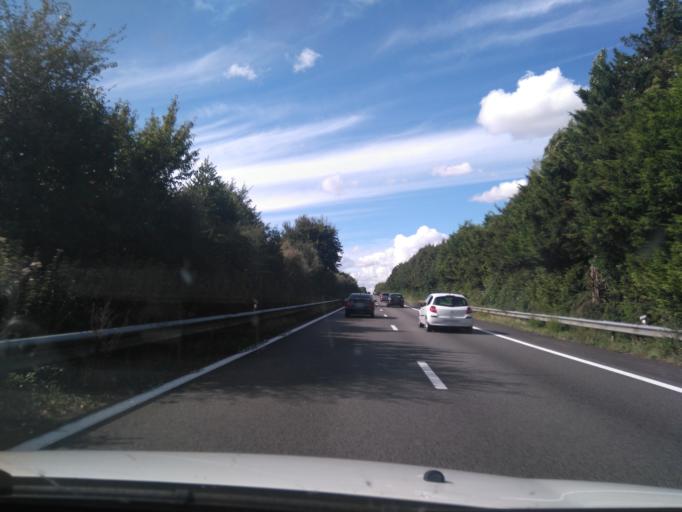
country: FR
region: Pays de la Loire
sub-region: Departement de la Loire-Atlantique
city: Jans
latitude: 47.6121
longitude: -1.6325
